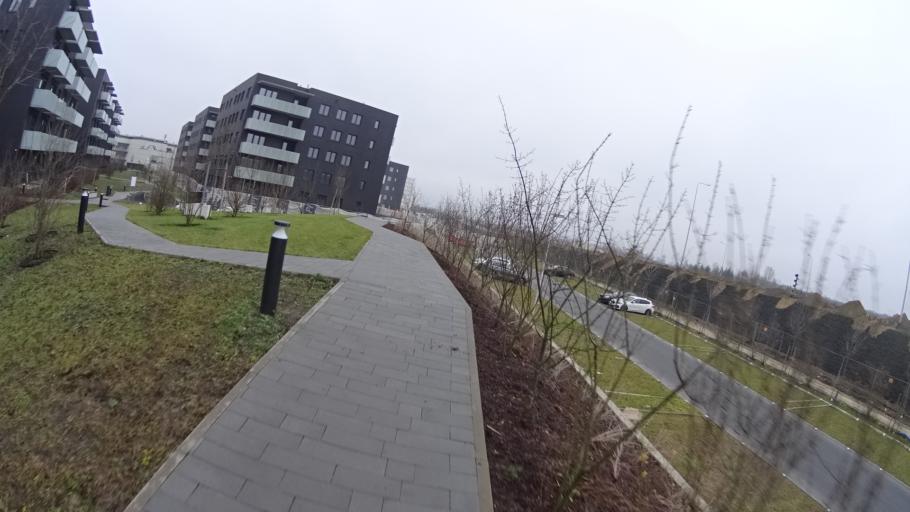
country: PL
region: Masovian Voivodeship
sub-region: Warszawa
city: Wilanow
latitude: 52.1538
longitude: 21.0748
